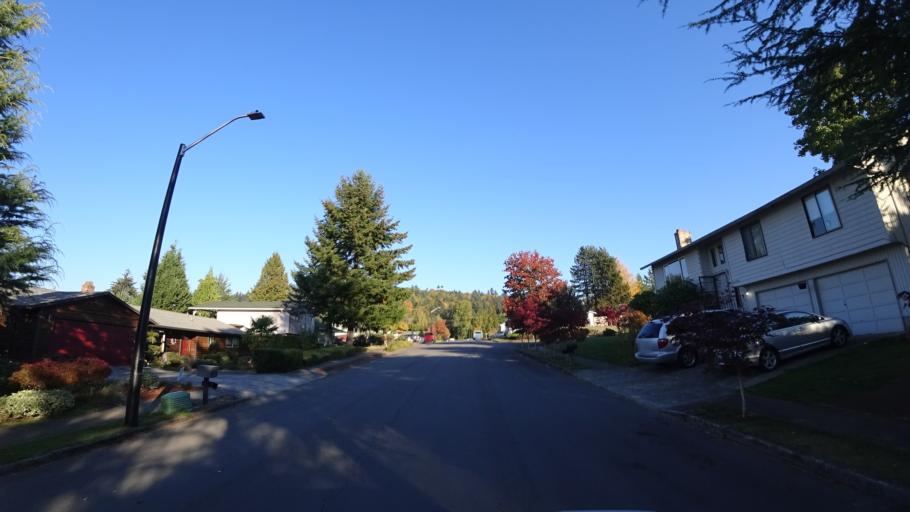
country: US
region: Oregon
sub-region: Multnomah County
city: Gresham
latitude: 45.4844
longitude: -122.4505
